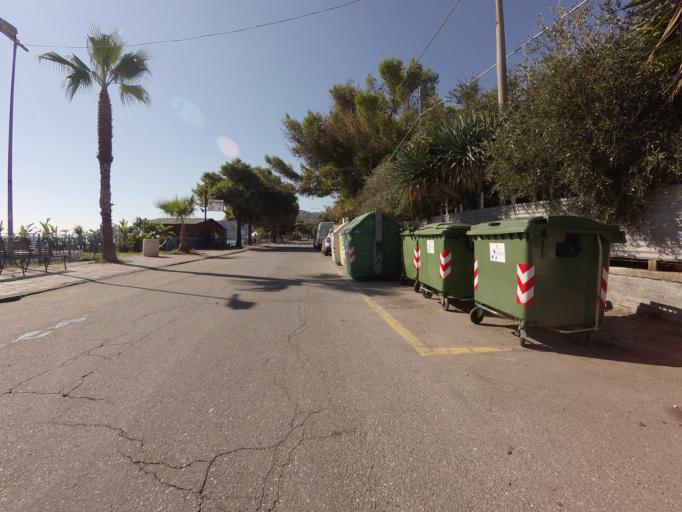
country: IT
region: Sicily
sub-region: Messina
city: Letojanni
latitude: 37.8730
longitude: 15.3017
